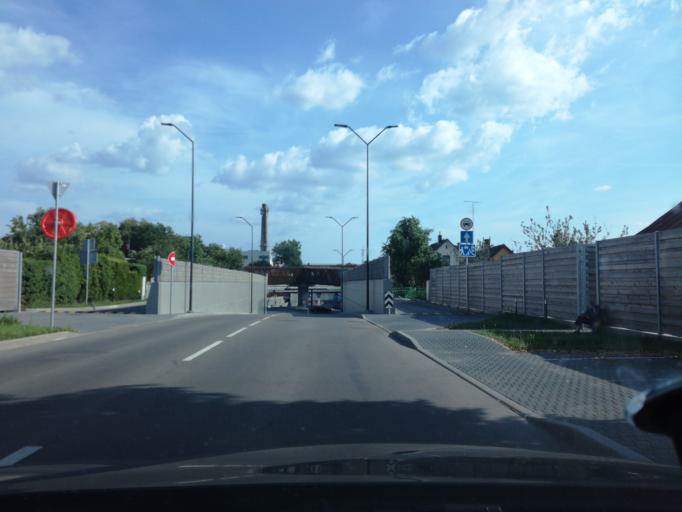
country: LT
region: Marijampoles apskritis
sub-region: Marijampole Municipality
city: Marijampole
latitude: 54.5398
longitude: 23.3502
